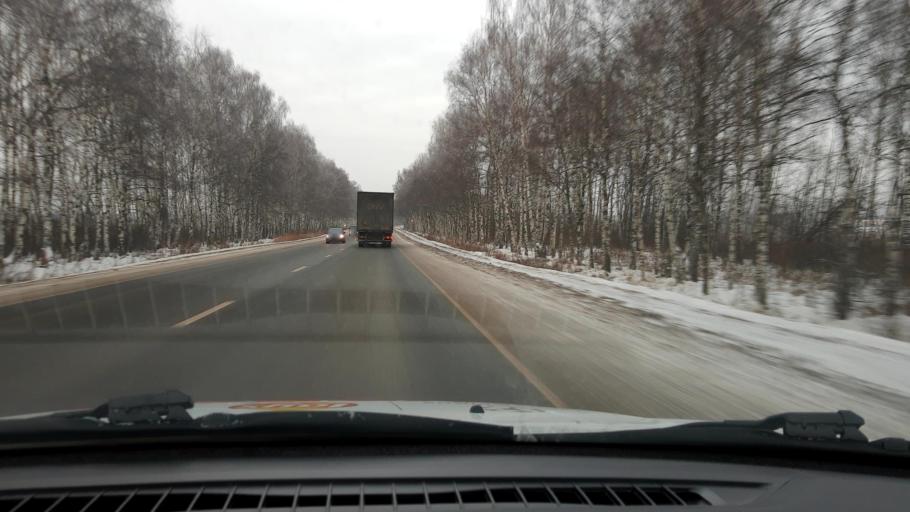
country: RU
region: Nizjnij Novgorod
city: Sitniki
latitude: 56.5336
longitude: 44.0228
